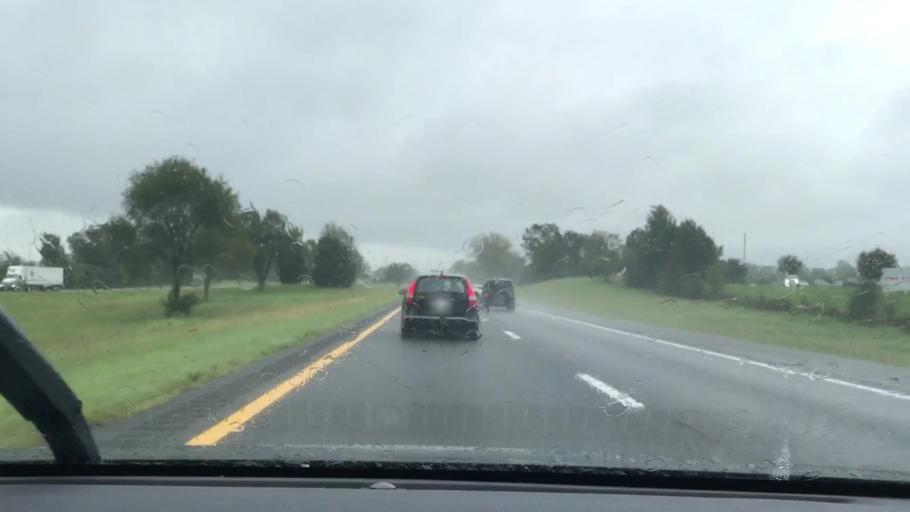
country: US
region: Tennessee
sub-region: Montgomery County
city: Clarksville
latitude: 36.5841
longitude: -87.2690
